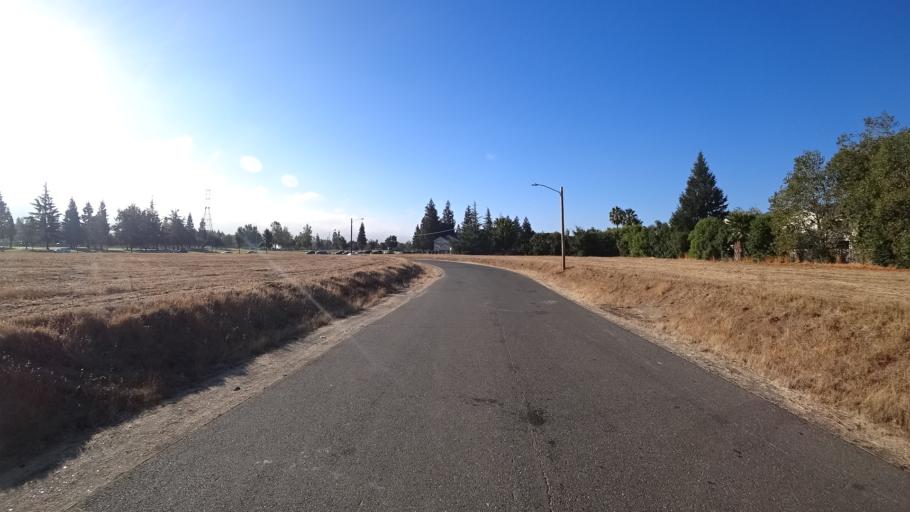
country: US
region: California
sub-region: Sacramento County
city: Laguna
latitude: 38.4450
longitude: -121.4291
